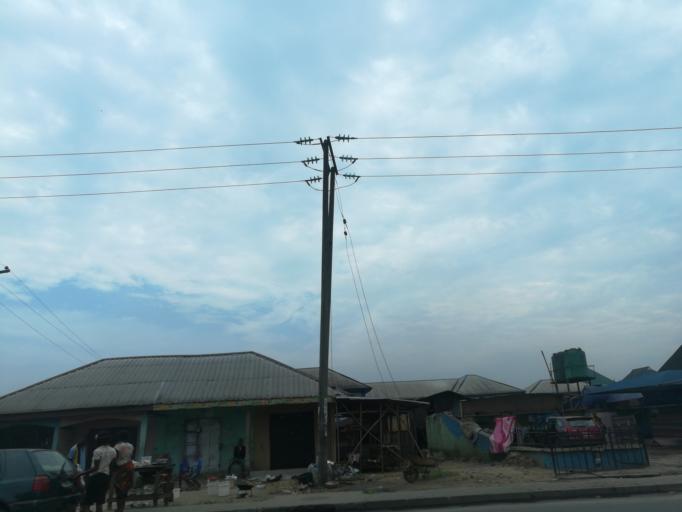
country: NG
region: Rivers
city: Port Harcourt
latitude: 4.8461
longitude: 6.9815
